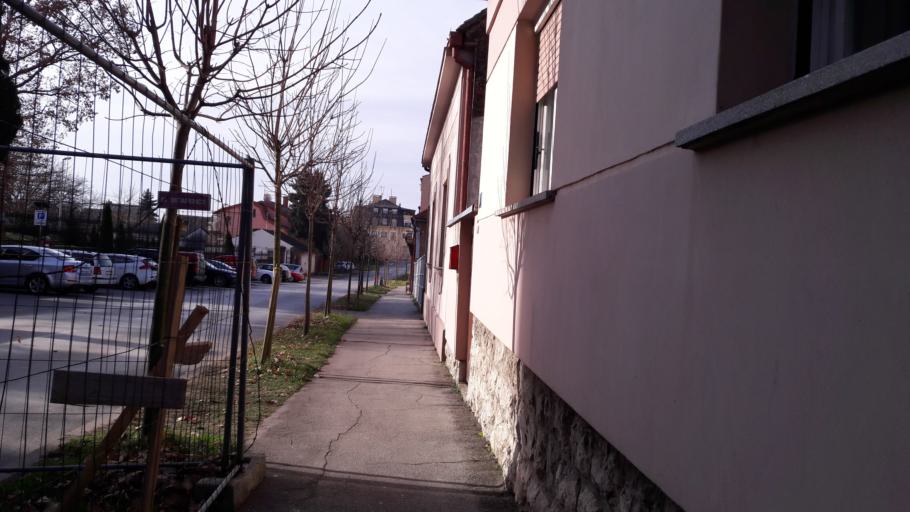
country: HR
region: Osjecko-Baranjska
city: Piskorevci
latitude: 45.3079
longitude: 18.4106
